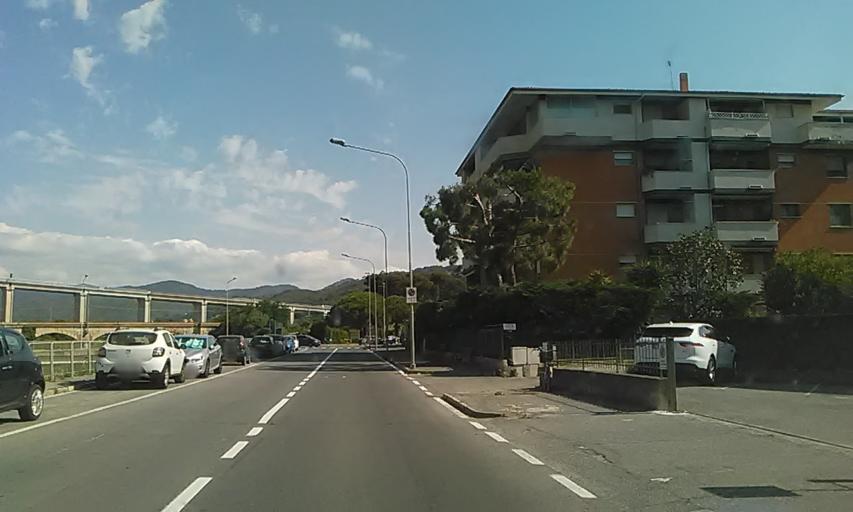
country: IT
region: Liguria
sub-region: Provincia di Savona
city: Andora
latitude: 43.9594
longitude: 8.1422
